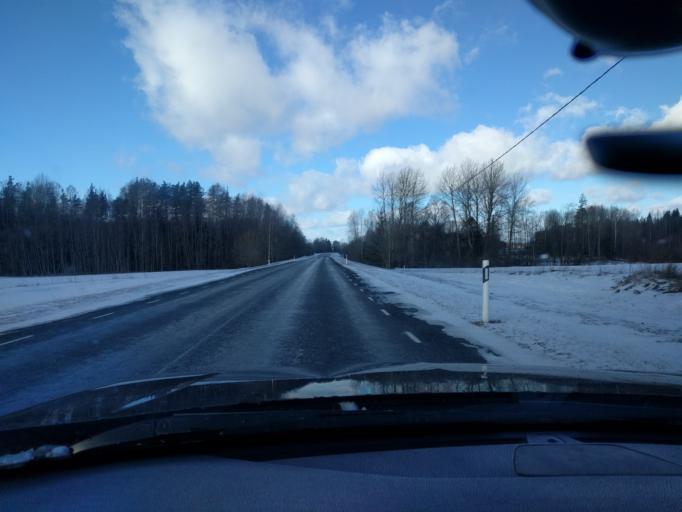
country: EE
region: Harju
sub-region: Anija vald
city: Kehra
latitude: 59.2246
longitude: 25.4039
